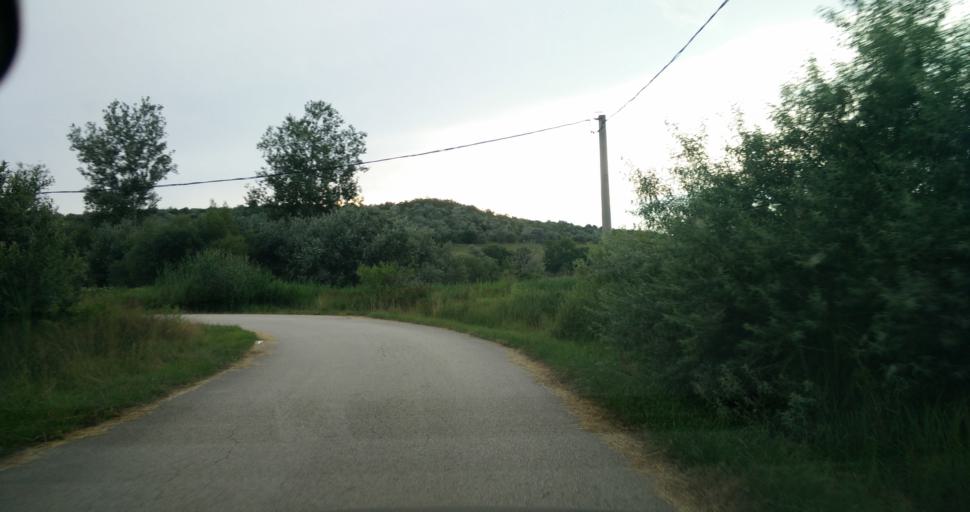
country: HU
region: Pest
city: Piliscsaba
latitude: 47.6425
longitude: 18.7868
